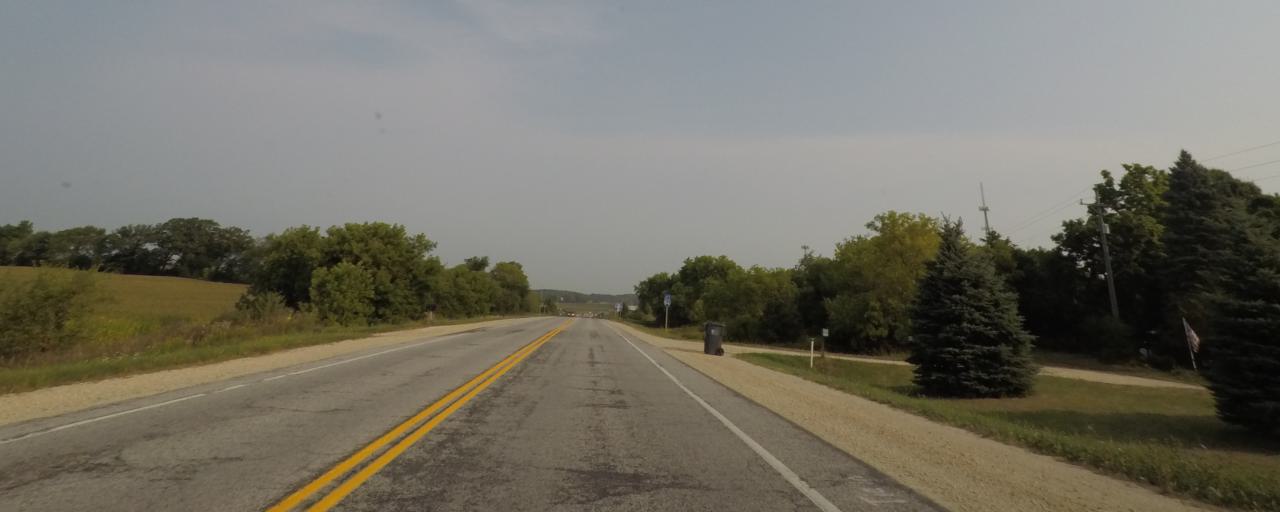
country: US
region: Wisconsin
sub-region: Dane County
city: Deerfield
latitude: 43.1047
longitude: -89.0814
